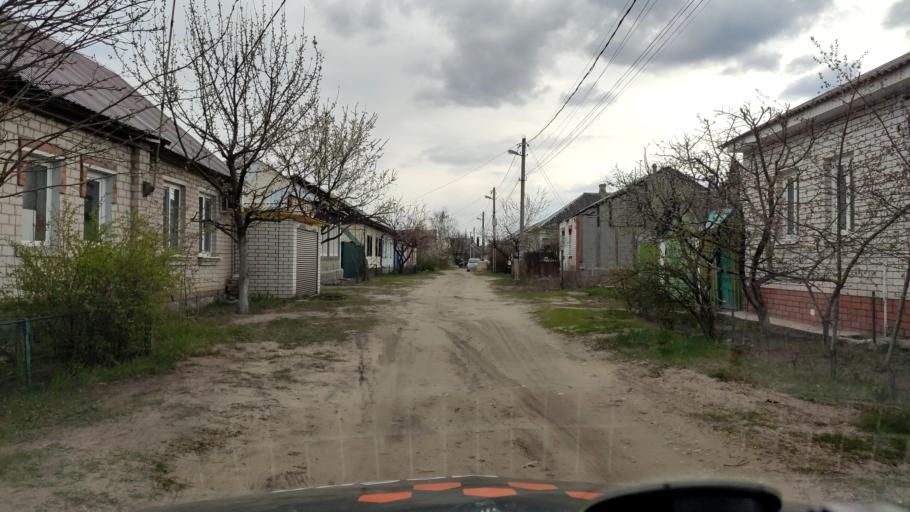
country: RU
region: Voronezj
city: Somovo
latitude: 51.7430
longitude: 39.2736
